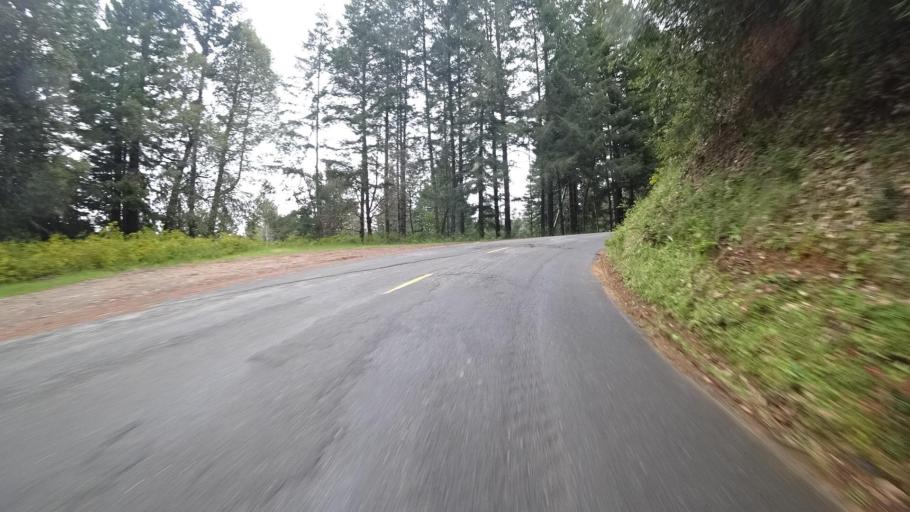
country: US
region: California
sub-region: Humboldt County
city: Redway
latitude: 40.2780
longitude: -123.7895
